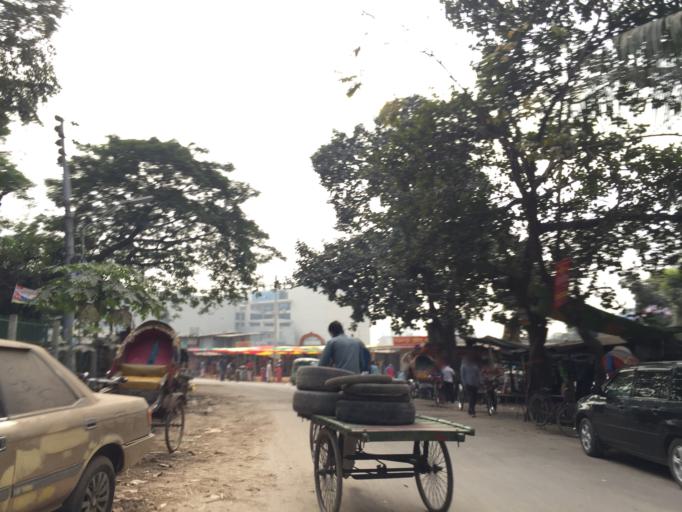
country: BD
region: Dhaka
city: Azimpur
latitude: 23.7791
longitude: 90.3710
